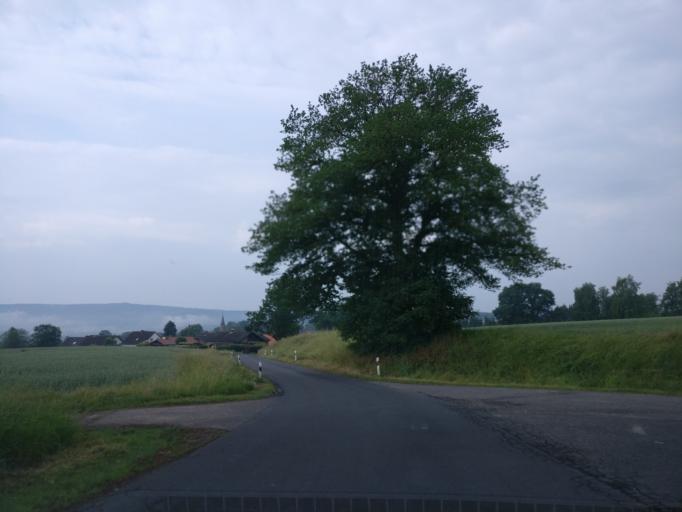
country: DE
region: Lower Saxony
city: Scheden
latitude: 51.4289
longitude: 9.7167
